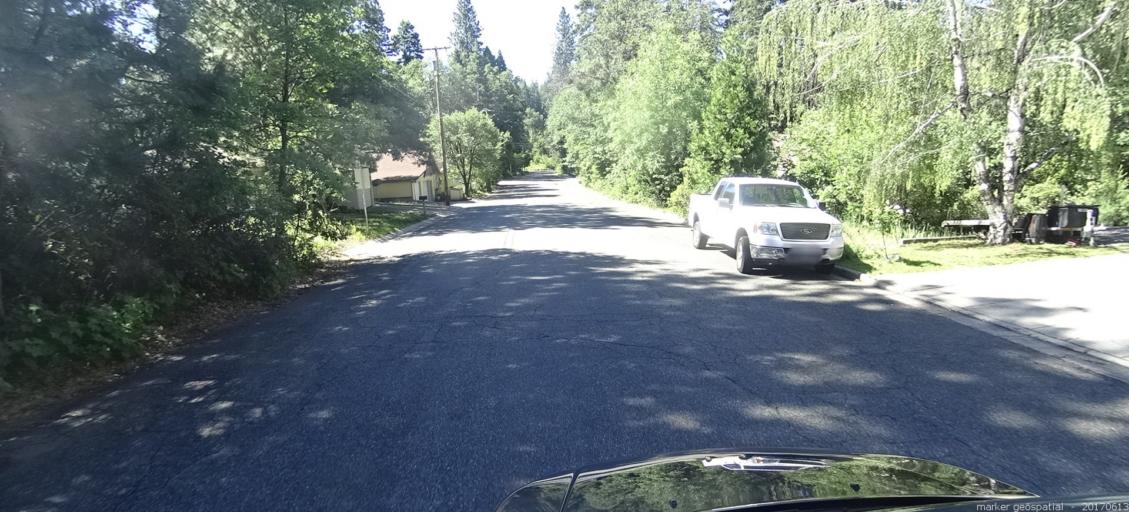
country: US
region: California
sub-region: Siskiyou County
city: Mount Shasta
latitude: 41.3132
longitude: -122.3021
